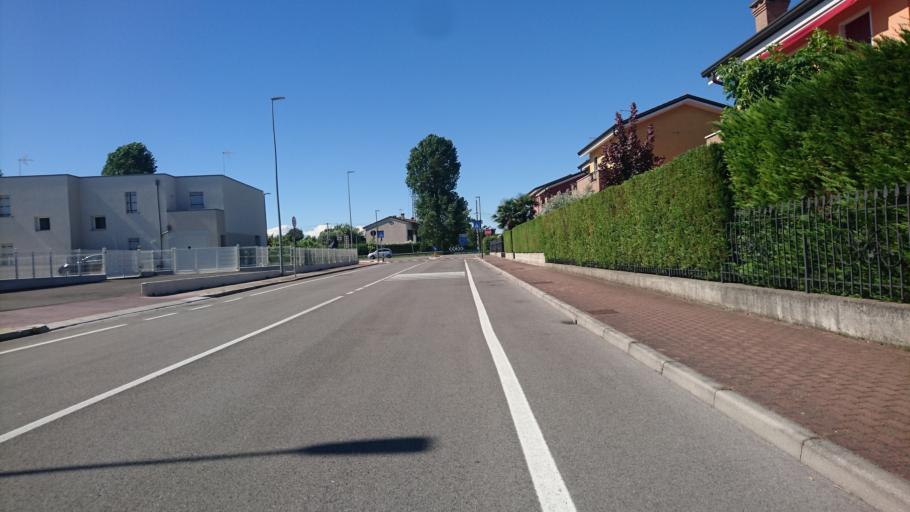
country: IT
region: Veneto
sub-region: Provincia di Padova
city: Sant'Angelo di Piove di Sacco
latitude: 45.3021
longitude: 12.0192
